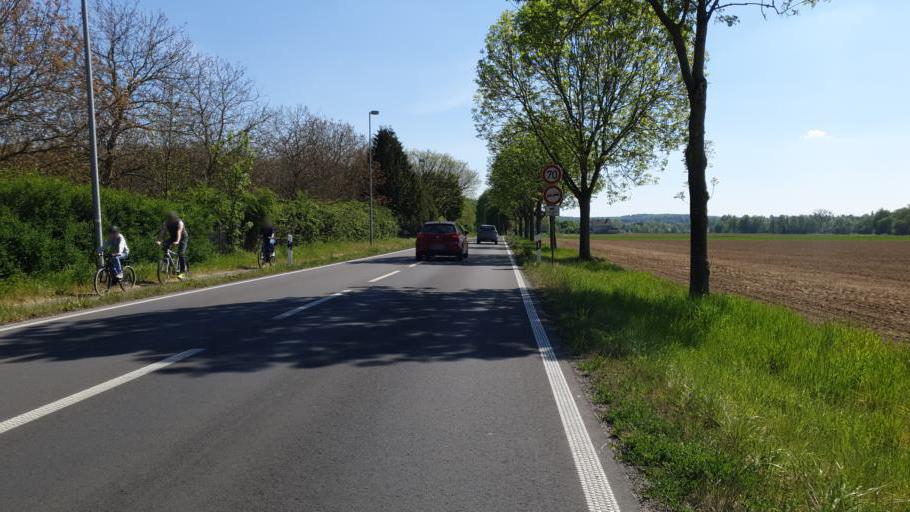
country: DE
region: North Rhine-Westphalia
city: Opladen
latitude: 51.0344
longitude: 7.0605
